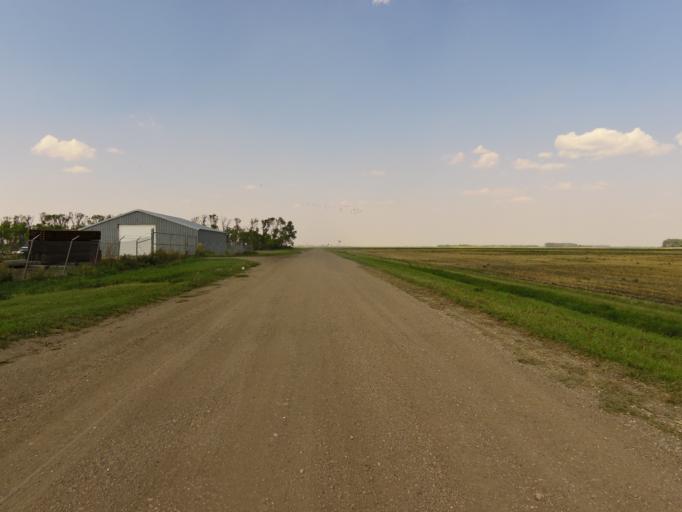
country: US
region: North Dakota
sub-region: Walsh County
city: Grafton
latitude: 48.4317
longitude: -97.3972
